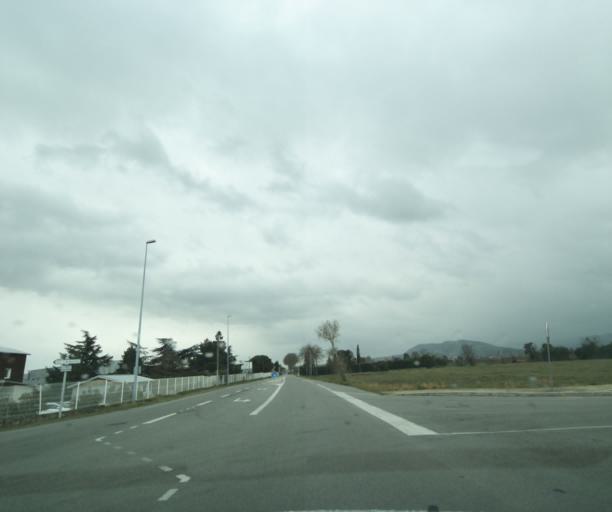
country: FR
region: Rhone-Alpes
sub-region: Departement de la Drome
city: Bourg-les-Valence
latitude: 44.9728
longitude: 4.8957
